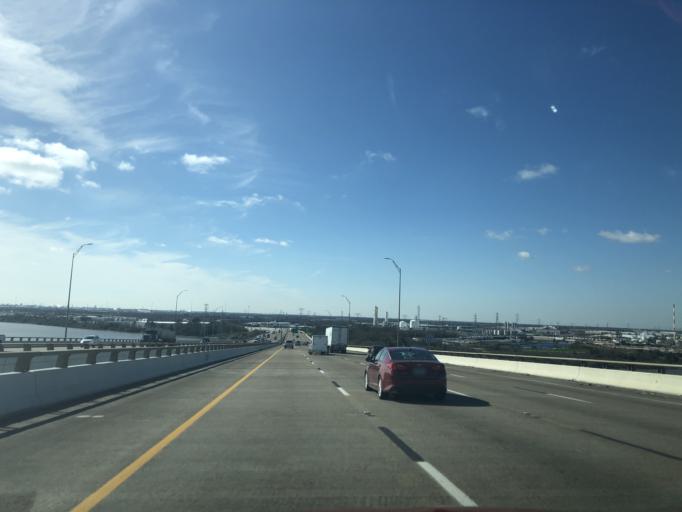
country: US
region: Texas
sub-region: Harris County
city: La Porte
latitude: 29.7007
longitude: -95.0204
